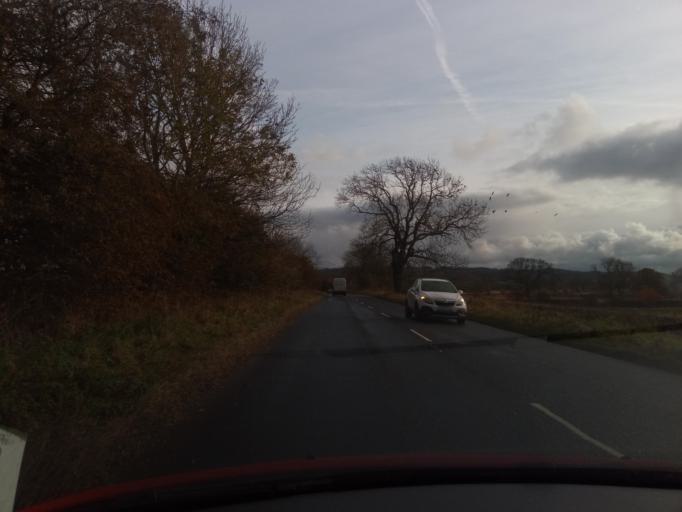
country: GB
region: England
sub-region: Northumberland
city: Wall
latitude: 55.0424
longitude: -2.1462
